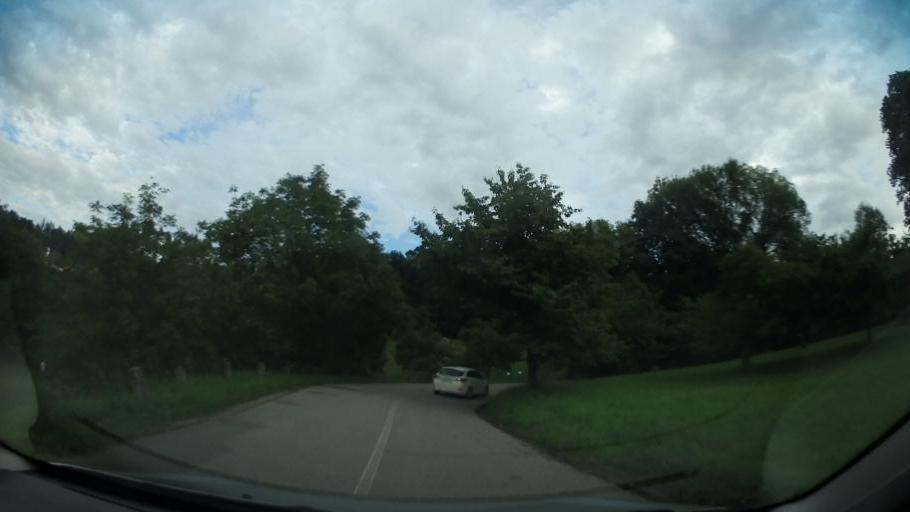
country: CZ
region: Olomoucky
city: Horni Stepanov
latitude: 49.5399
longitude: 16.7200
